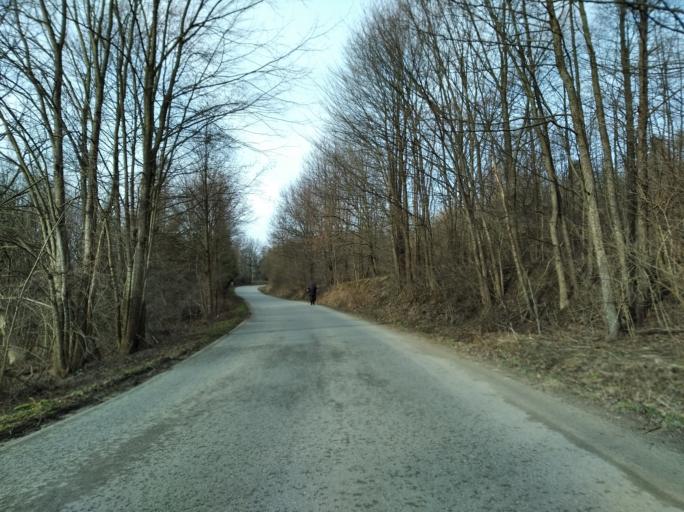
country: PL
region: Subcarpathian Voivodeship
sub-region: Powiat brzozowski
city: Turze Pole
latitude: 49.6743
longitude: 22.0035
